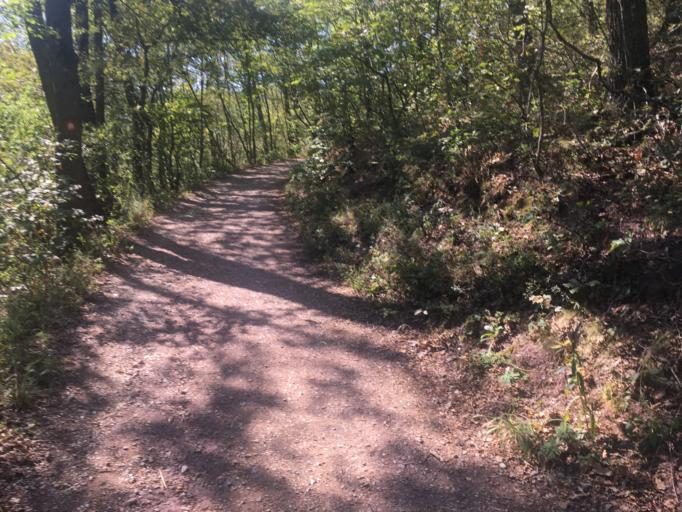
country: XK
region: Pristina
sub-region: Komuna e Prishtines
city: Pristina
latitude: 42.6654
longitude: 21.2194
